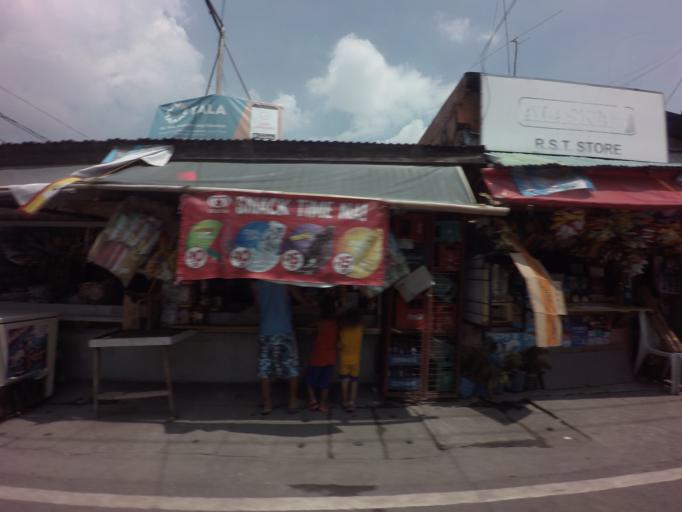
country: PH
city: Sambayanihan People's Village
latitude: 14.4410
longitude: 121.0506
